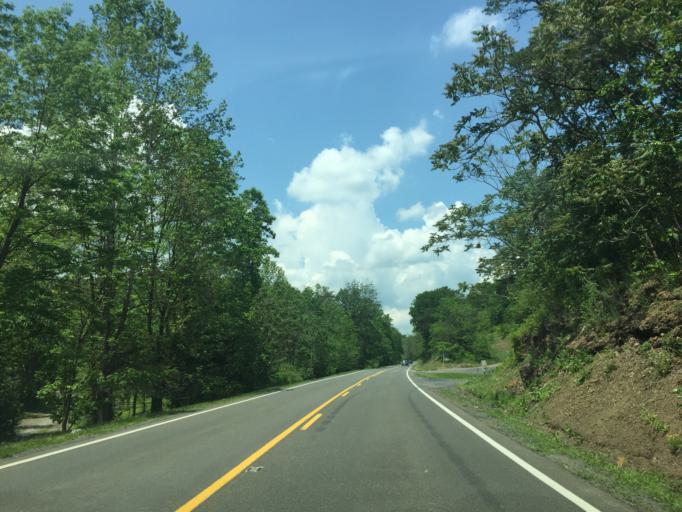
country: US
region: Virginia
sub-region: Shenandoah County
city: Strasburg
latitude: 39.0780
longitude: -78.3798
